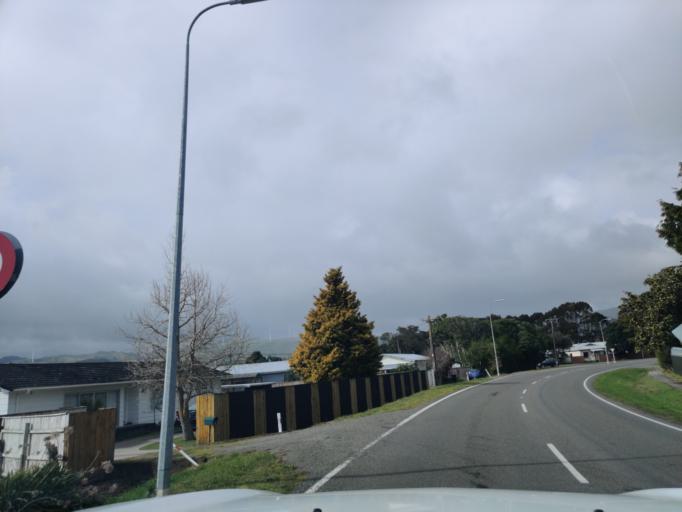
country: NZ
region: Manawatu-Wanganui
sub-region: Palmerston North City
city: Palmerston North
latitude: -40.2942
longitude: 175.7523
